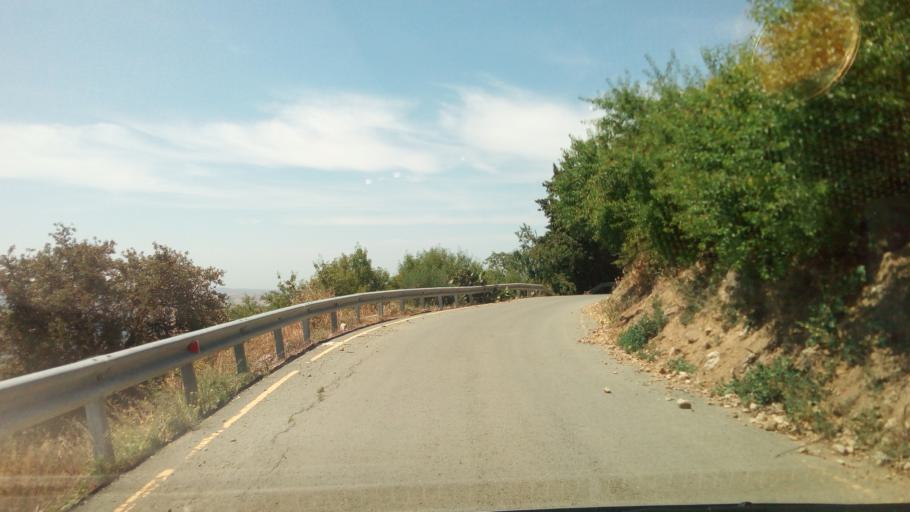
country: CY
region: Pafos
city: Mesogi
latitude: 34.8532
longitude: 32.6183
